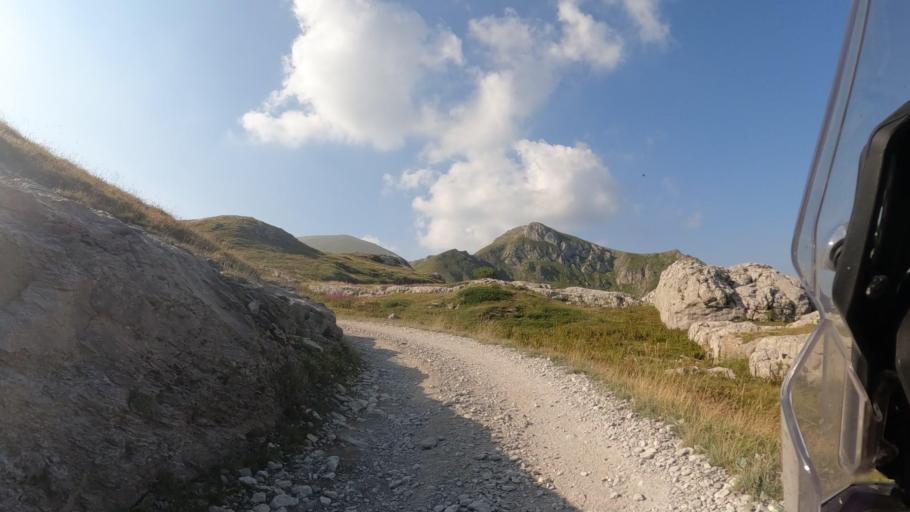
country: IT
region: Piedmont
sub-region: Provincia di Cuneo
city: Limone Piemonte
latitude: 44.1614
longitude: 7.6696
